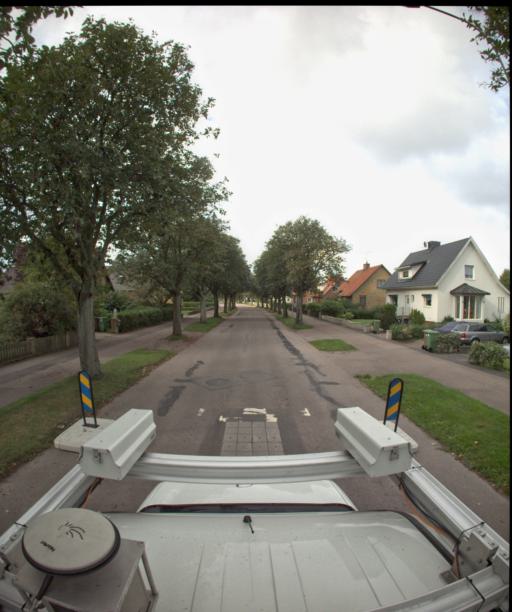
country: SE
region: Halland
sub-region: Falkenbergs Kommun
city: Falkenberg
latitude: 56.8918
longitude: 12.5026
